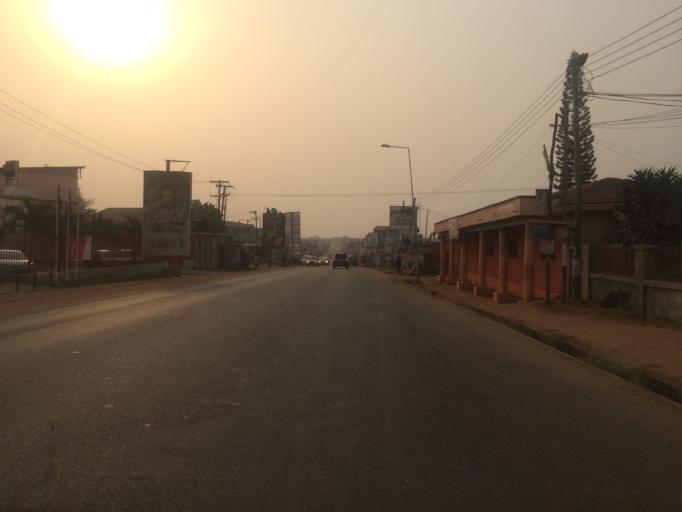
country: GH
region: Greater Accra
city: Nungua
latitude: 5.6433
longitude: -0.1109
